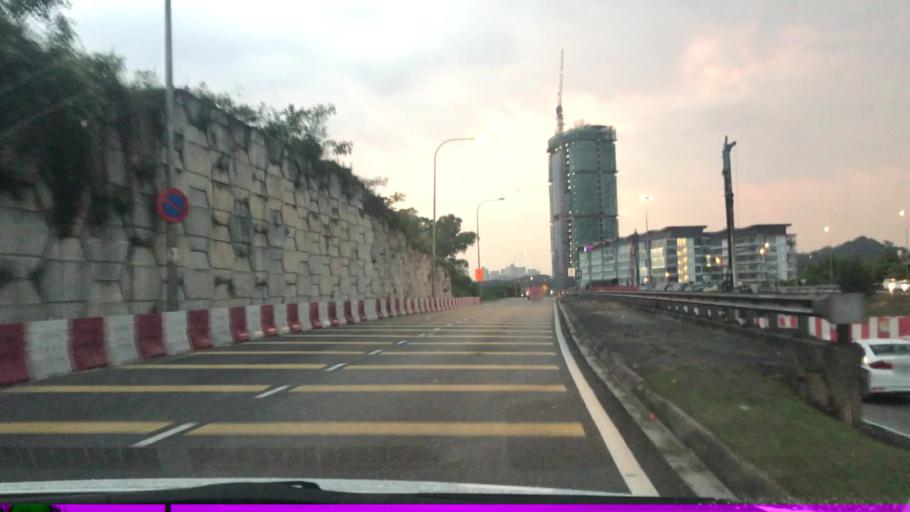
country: MY
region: Selangor
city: Kampong Baharu Balakong
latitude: 3.0761
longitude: 101.7148
